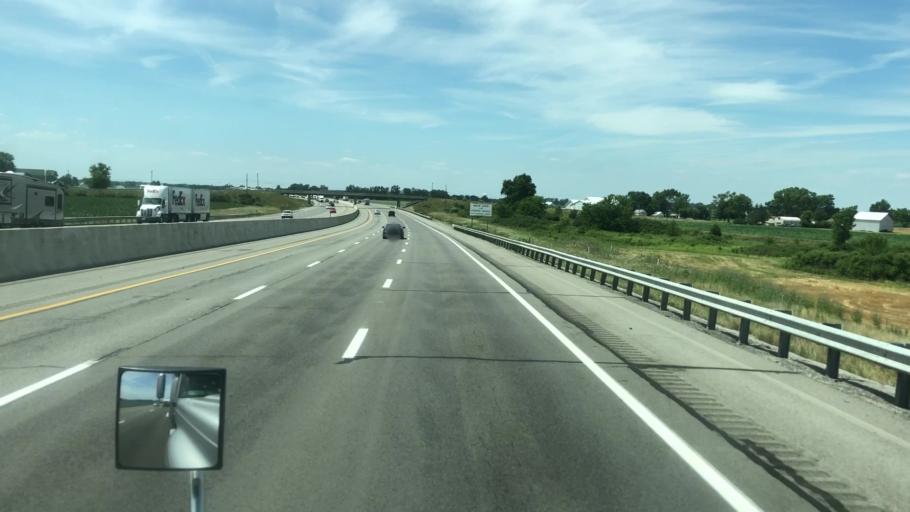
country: US
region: Ohio
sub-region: Wood County
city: Walbridge
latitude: 41.5360
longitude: -83.4878
